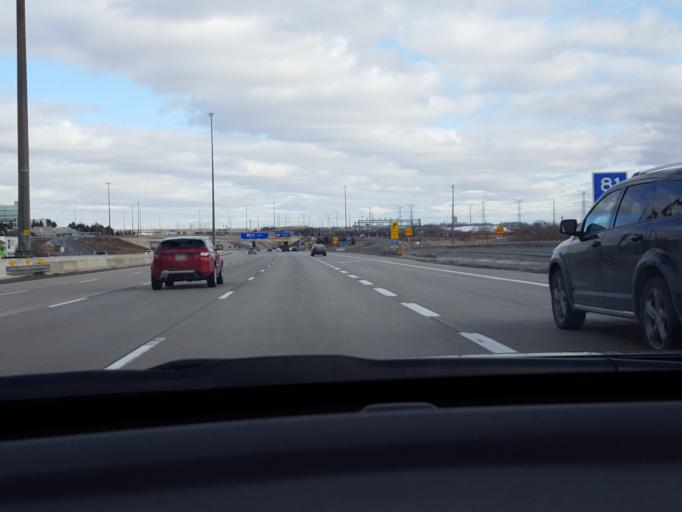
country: CA
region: Ontario
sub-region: York
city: Richmond Hill
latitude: 43.8365
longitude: -79.3879
